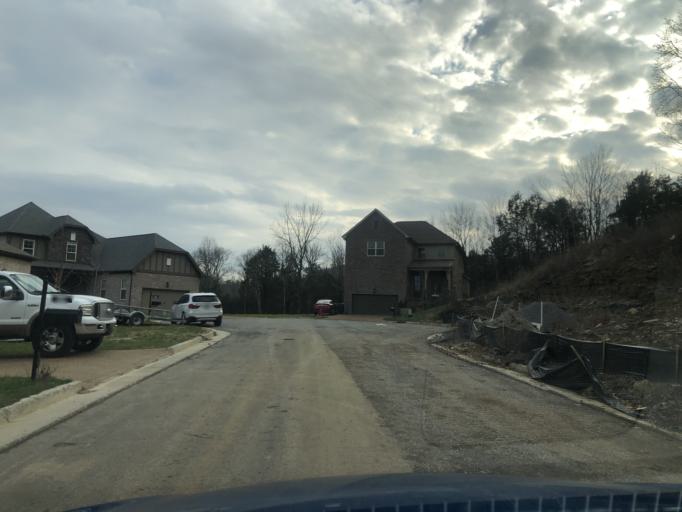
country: US
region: Tennessee
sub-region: Davidson County
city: Belle Meade
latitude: 36.1024
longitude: -86.9356
